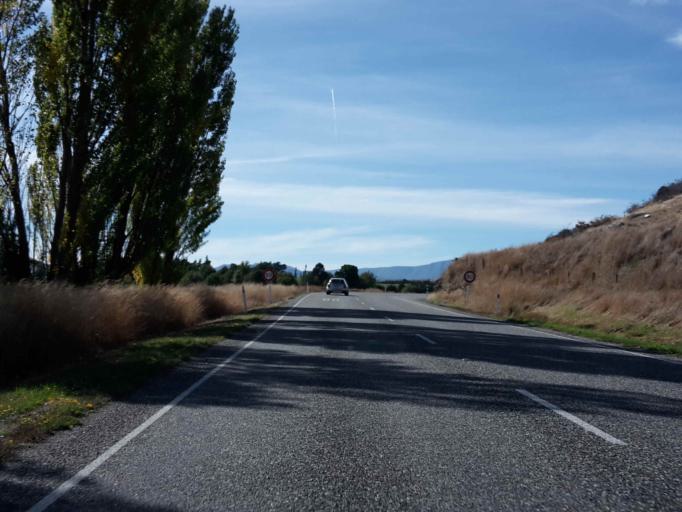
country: NZ
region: Otago
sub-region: Queenstown-Lakes District
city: Wanaka
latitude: -44.8383
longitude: 169.4069
